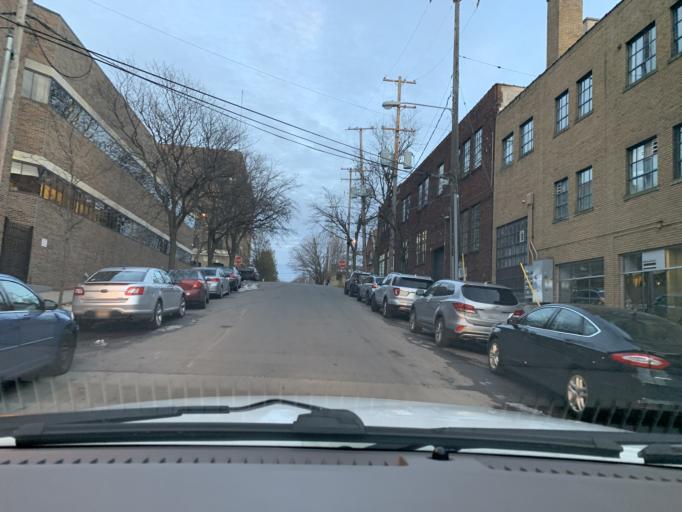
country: US
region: Michigan
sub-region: Kent County
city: Grand Rapids
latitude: 42.9609
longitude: -85.6676
